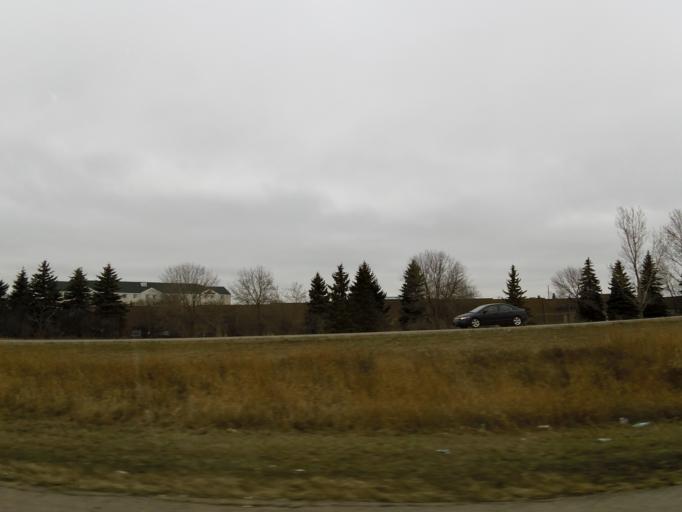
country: US
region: Minnesota
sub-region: Dakota County
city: Eagan
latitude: 44.7882
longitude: -93.2039
